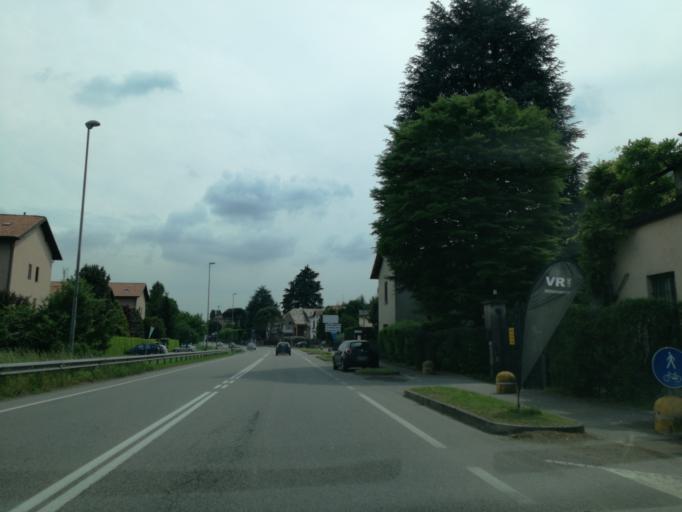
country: IT
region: Lombardy
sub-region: Provincia di Monza e Brianza
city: Albiate
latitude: 45.6613
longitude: 9.2496
